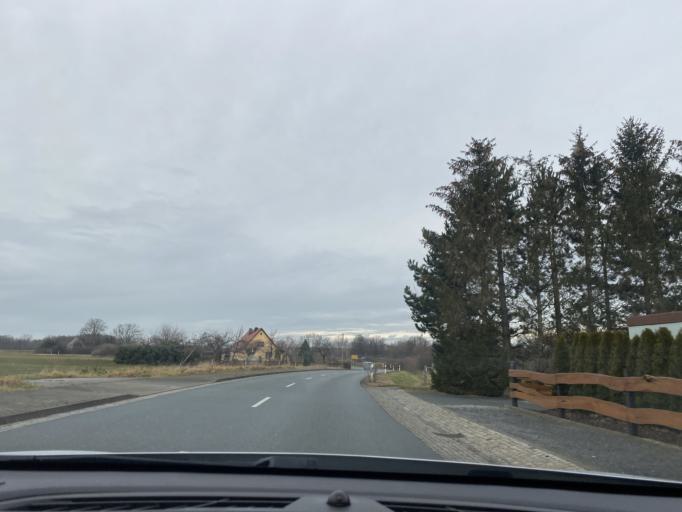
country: DE
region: Saxony
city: Sohland am Rotstein
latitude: 51.1344
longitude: 14.7706
